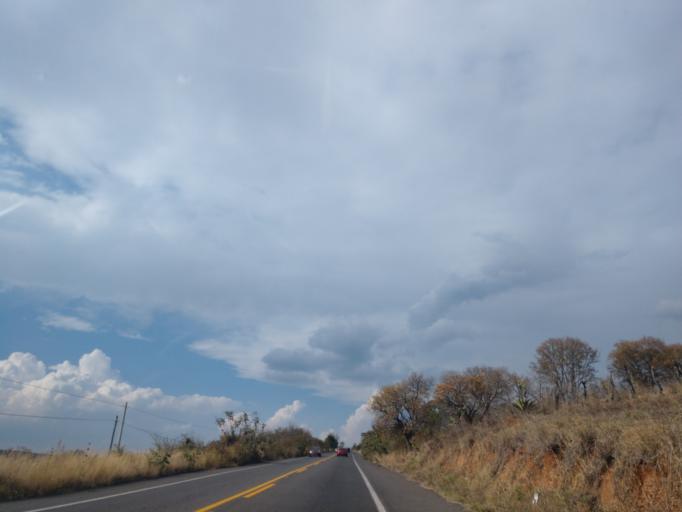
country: MX
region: Jalisco
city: La Manzanilla de la Paz
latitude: 20.0636
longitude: -103.1716
